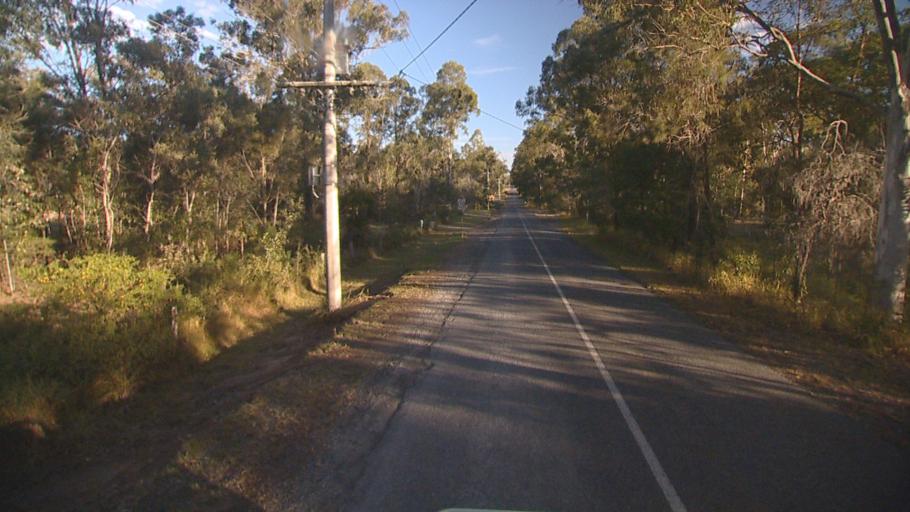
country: AU
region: Queensland
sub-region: Logan
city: Waterford West
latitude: -27.7271
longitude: 153.1470
